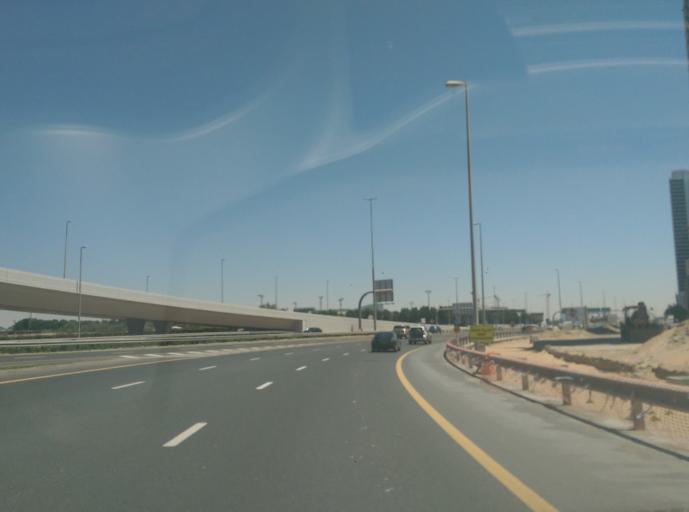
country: AE
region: Dubai
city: Dubai
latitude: 25.1033
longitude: 55.1782
